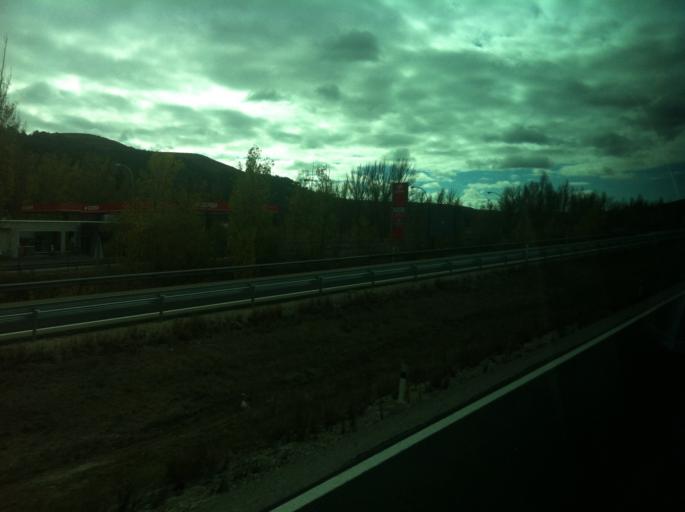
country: ES
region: Castille and Leon
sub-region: Provincia de Burgos
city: Briviesca
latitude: 42.5268
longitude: -3.3341
